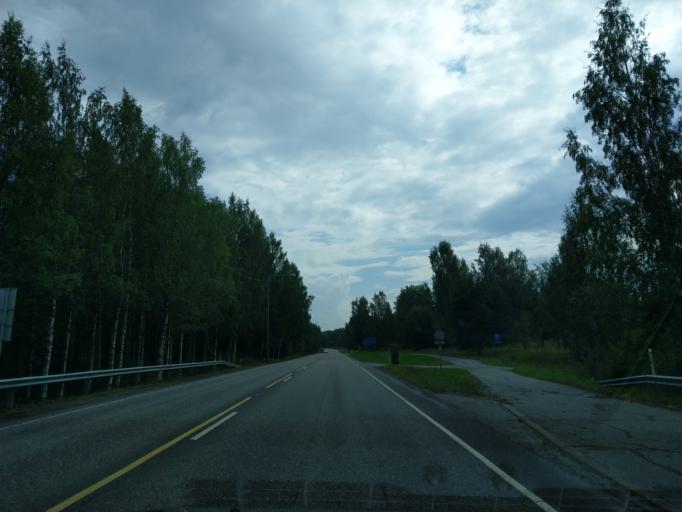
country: FI
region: South Karelia
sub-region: Imatra
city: Parikkala
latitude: 61.5997
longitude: 29.4830
